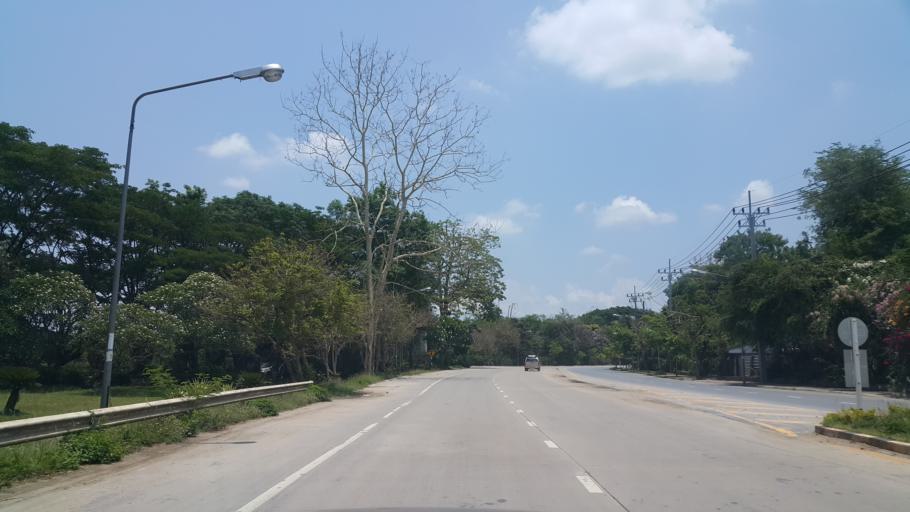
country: TH
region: Chiang Rai
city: Chiang Rai
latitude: 19.9213
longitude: 99.8198
